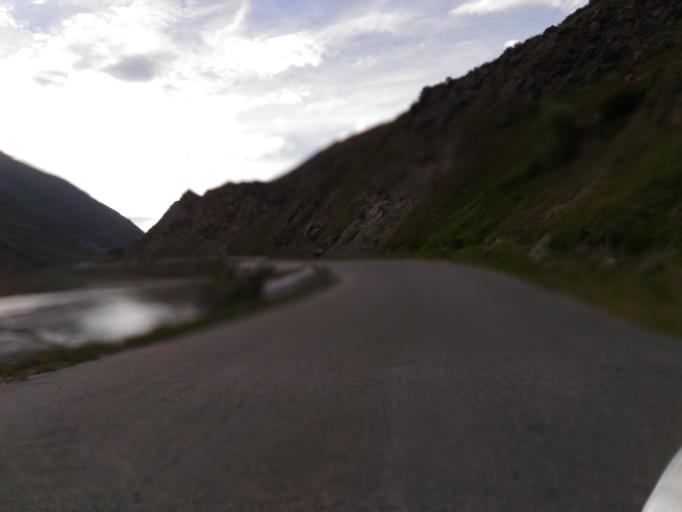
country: IN
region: Himachal Pradesh
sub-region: Lahul and Spiti
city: Kyelang
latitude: 32.4560
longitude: 77.1469
